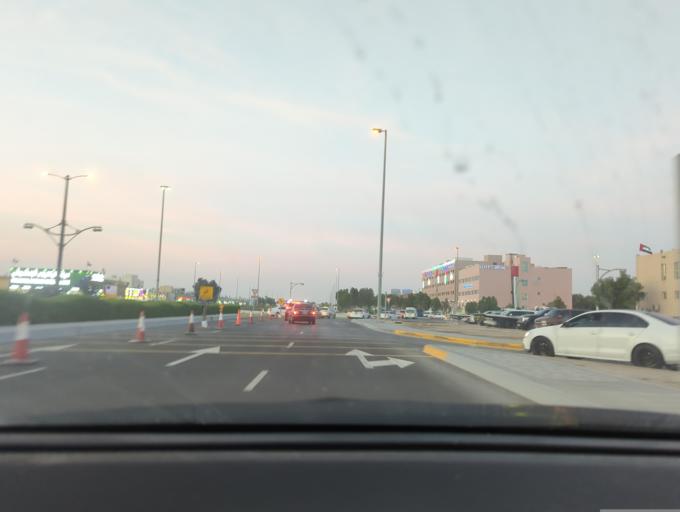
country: AE
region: Abu Dhabi
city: Abu Dhabi
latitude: 24.3770
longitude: 54.5160
